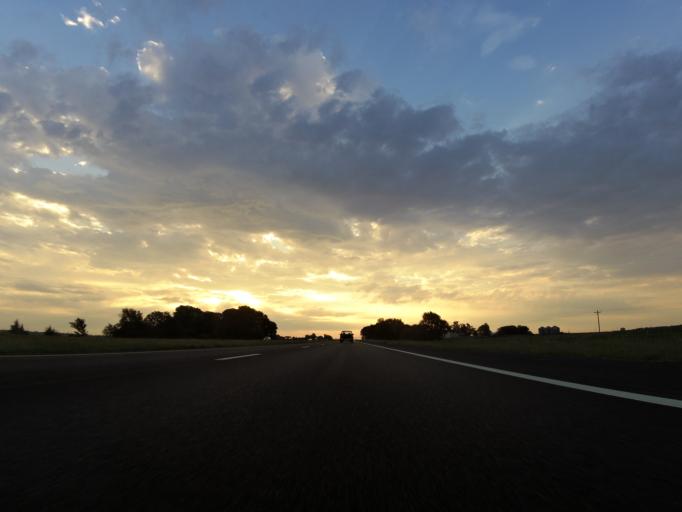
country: US
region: Kansas
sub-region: Sedgwick County
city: Colwich
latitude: 37.8259
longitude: -97.5487
